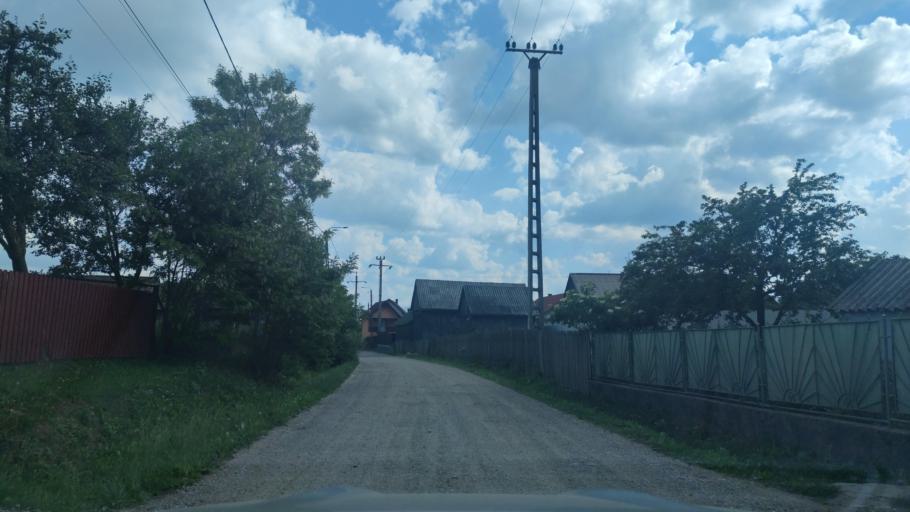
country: RO
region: Harghita
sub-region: Comuna Remetea
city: Remetea
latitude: 46.7971
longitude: 25.4435
